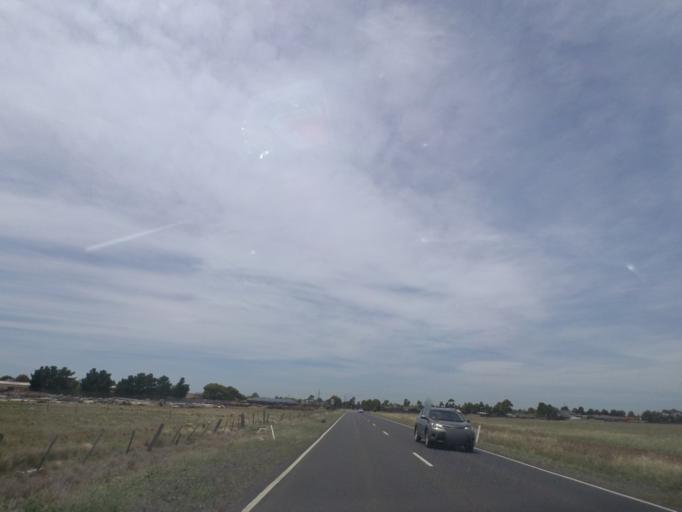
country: AU
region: Victoria
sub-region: Melton
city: Caroline Springs
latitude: -37.7439
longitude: 144.7211
